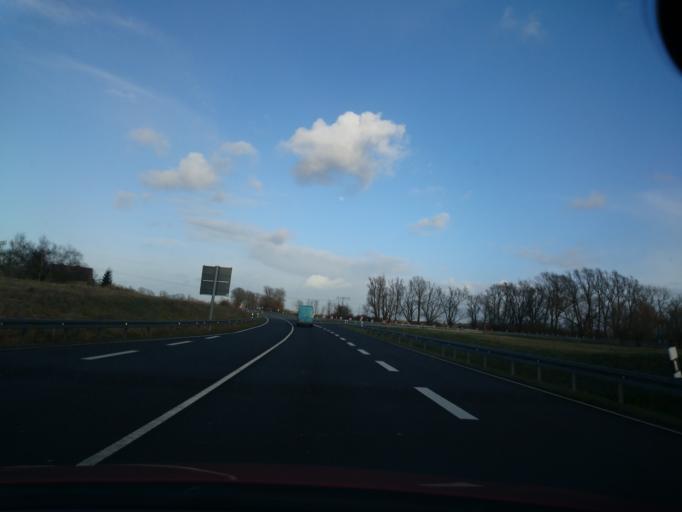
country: DE
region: Mecklenburg-Vorpommern
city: Weitenhagen
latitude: 54.0606
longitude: 13.3792
